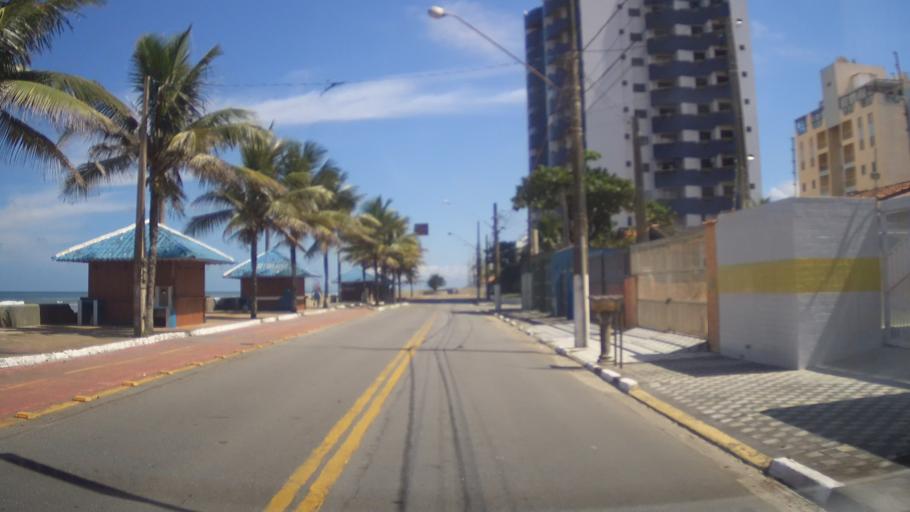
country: BR
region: Sao Paulo
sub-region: Mongagua
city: Mongagua
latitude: -24.1043
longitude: -46.6360
